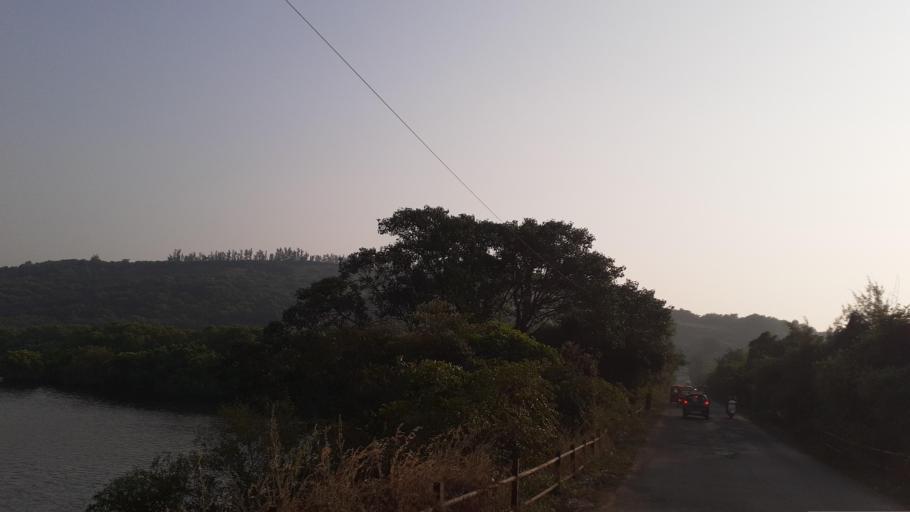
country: IN
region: Maharashtra
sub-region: Ratnagiri
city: Ratnagiri
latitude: 17.0398
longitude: 73.2966
